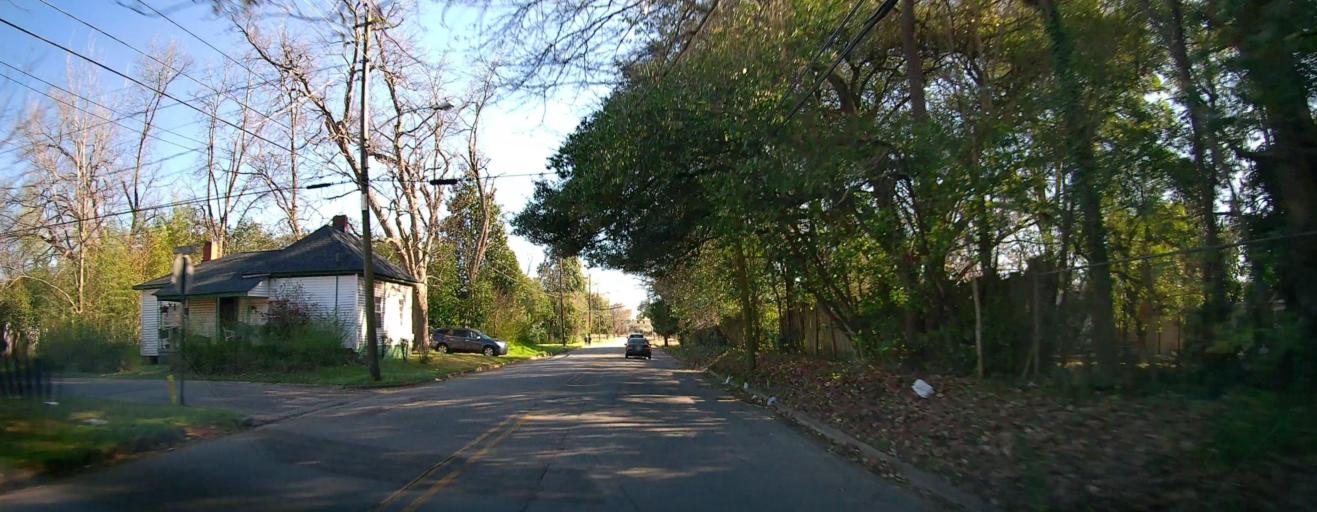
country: US
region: Georgia
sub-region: Peach County
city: Fort Valley
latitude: 32.5613
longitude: -83.8933
